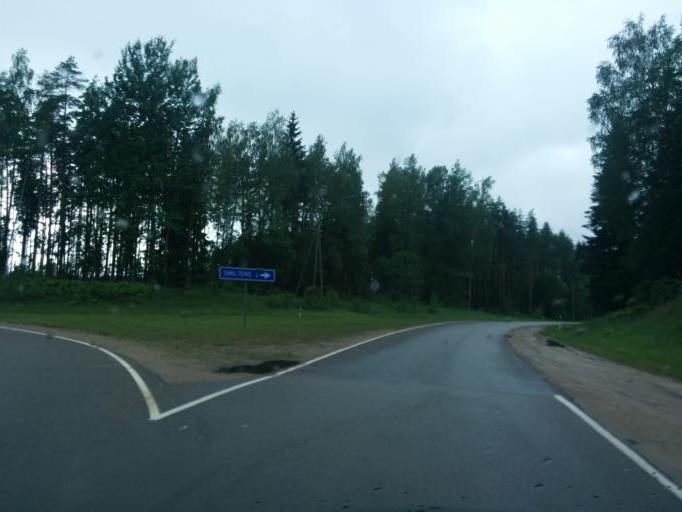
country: LV
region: Smiltene
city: Smiltene
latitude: 57.3894
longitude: 25.9750
